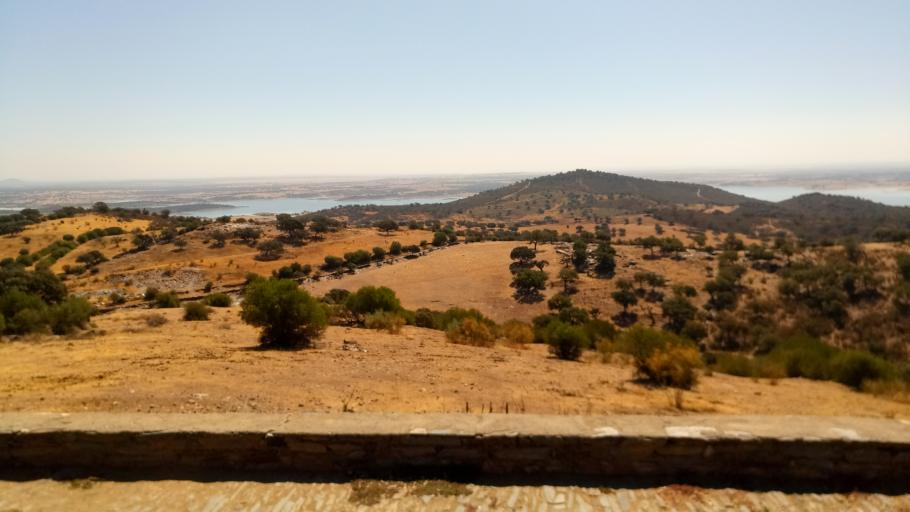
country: PT
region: Evora
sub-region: Mourao
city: Mourao
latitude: 38.4419
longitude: -7.3791
